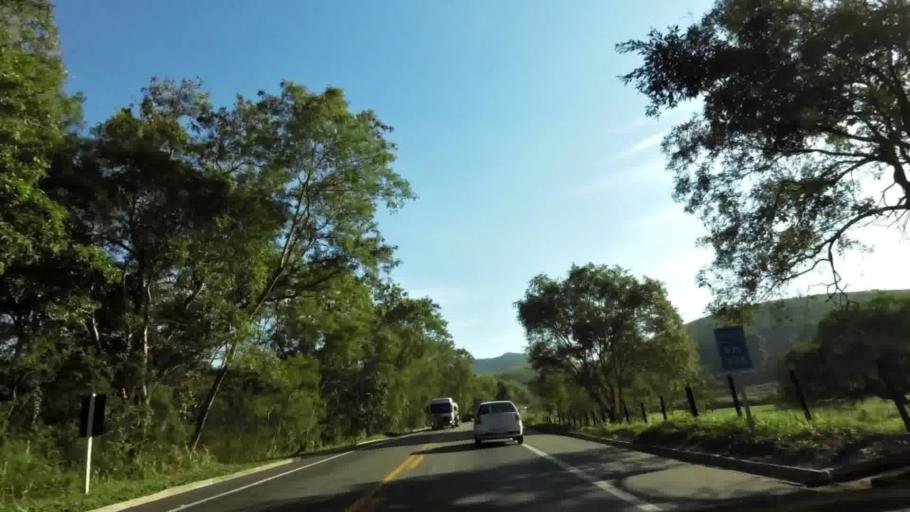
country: BR
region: Espirito Santo
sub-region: Viana
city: Viana
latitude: -20.4084
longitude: -40.4584
